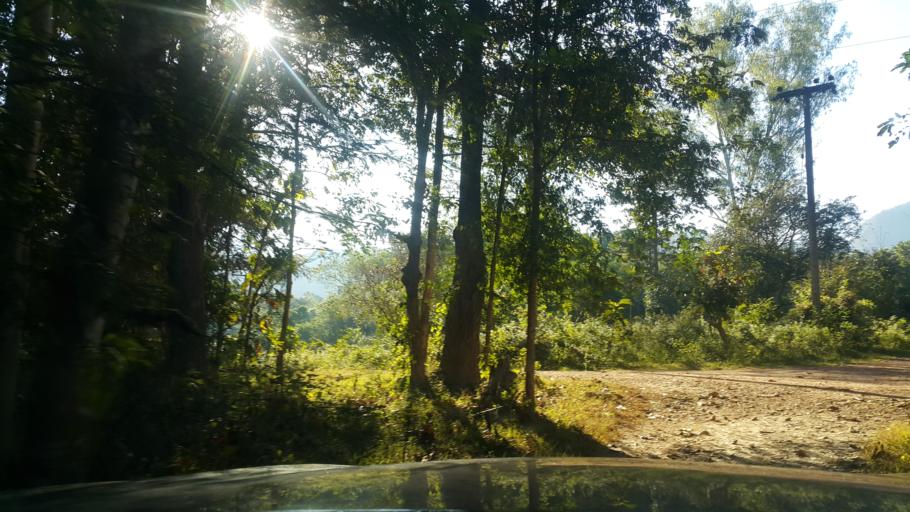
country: TH
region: Chiang Mai
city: Mae On
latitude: 18.6966
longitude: 99.2034
